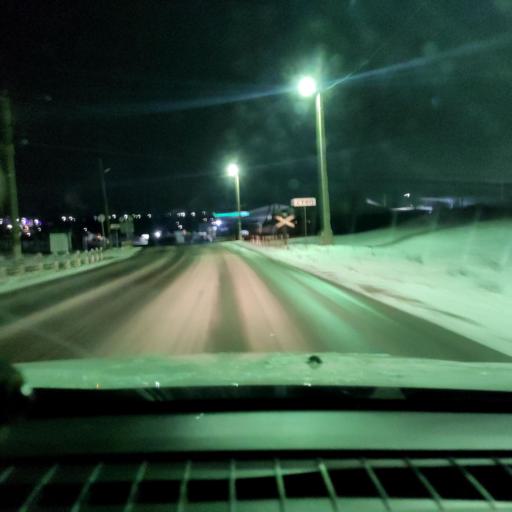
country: RU
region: Samara
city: Kurumoch
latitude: 53.4805
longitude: 50.0506
